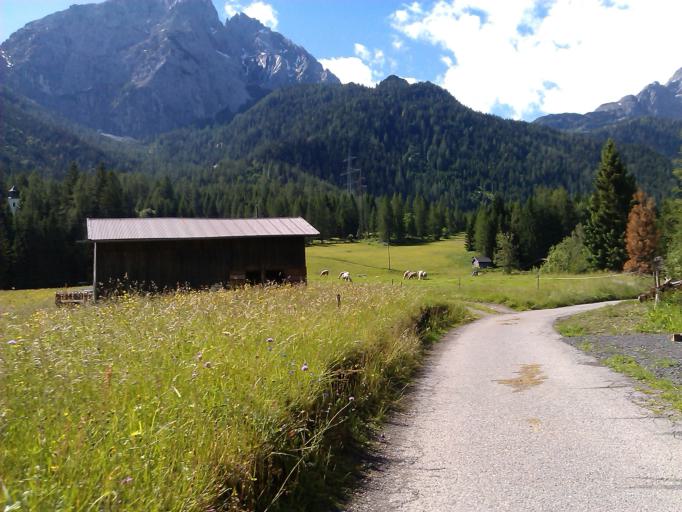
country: AT
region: Tyrol
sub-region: Politischer Bezirk Reutte
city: Biberwier
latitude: 47.3804
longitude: 10.8945
